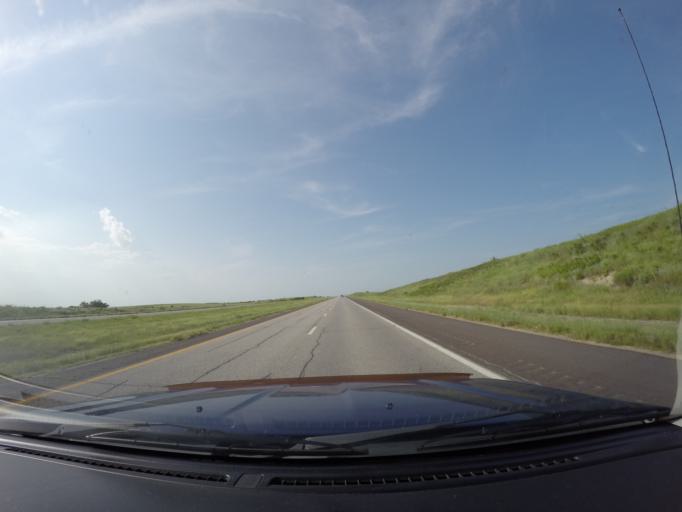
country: US
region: Kansas
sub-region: Riley County
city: Manhattan
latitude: 39.1249
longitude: -96.5381
